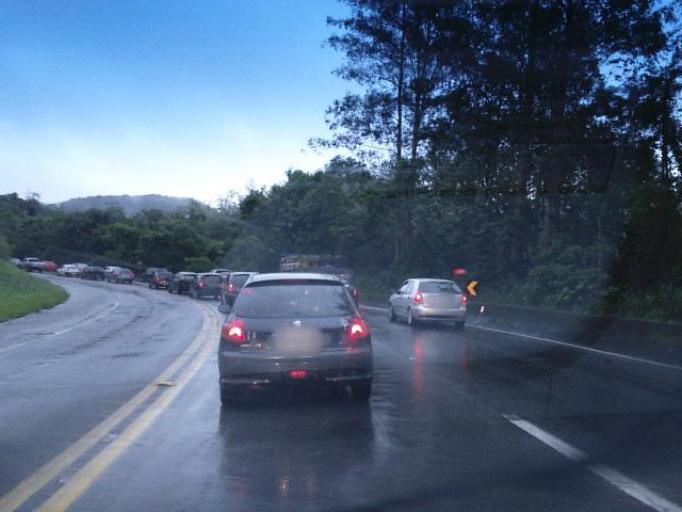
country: BR
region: Sao Paulo
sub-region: Juquitiba
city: Juquitiba
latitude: -24.0986
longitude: -47.2544
